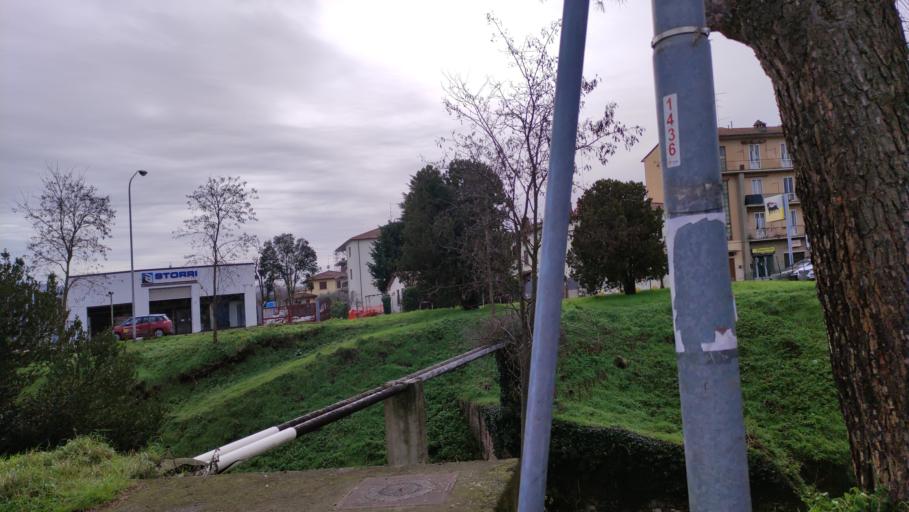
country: IT
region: Tuscany
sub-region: Province of Arezzo
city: Arezzo
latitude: 43.4707
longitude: 11.8667
